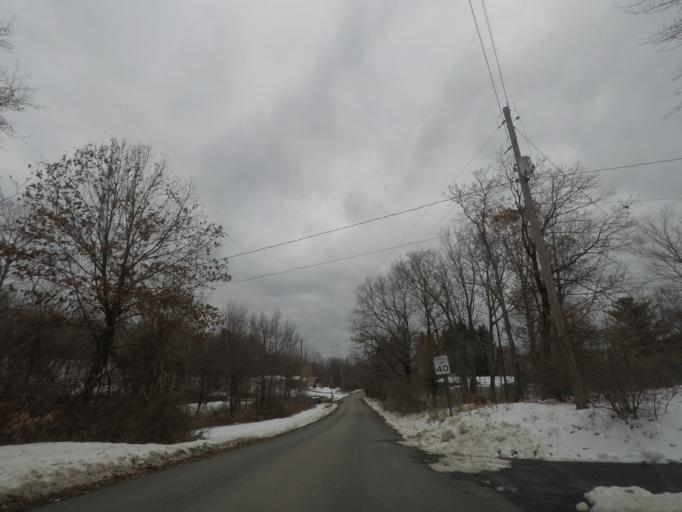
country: US
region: New York
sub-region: Rensselaer County
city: West Sand Lake
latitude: 42.6079
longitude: -73.6306
